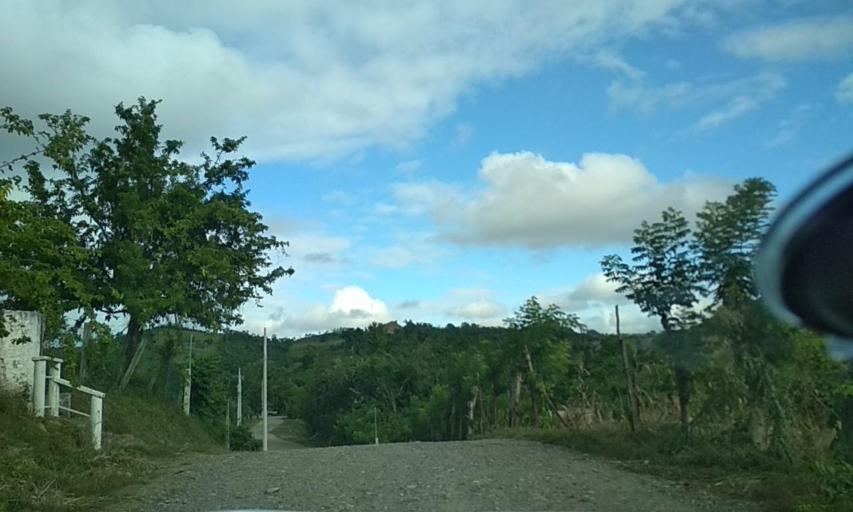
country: MX
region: Veracruz
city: Cazones de Herrera
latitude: 20.6478
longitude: -97.3405
